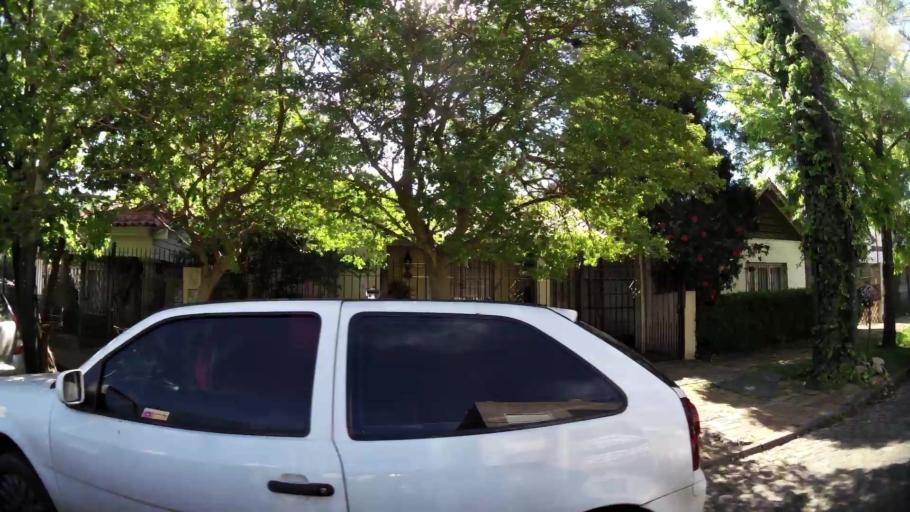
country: AR
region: Buenos Aires
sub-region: Partido de Lomas de Zamora
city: Lomas de Zamora
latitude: -34.7571
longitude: -58.4065
